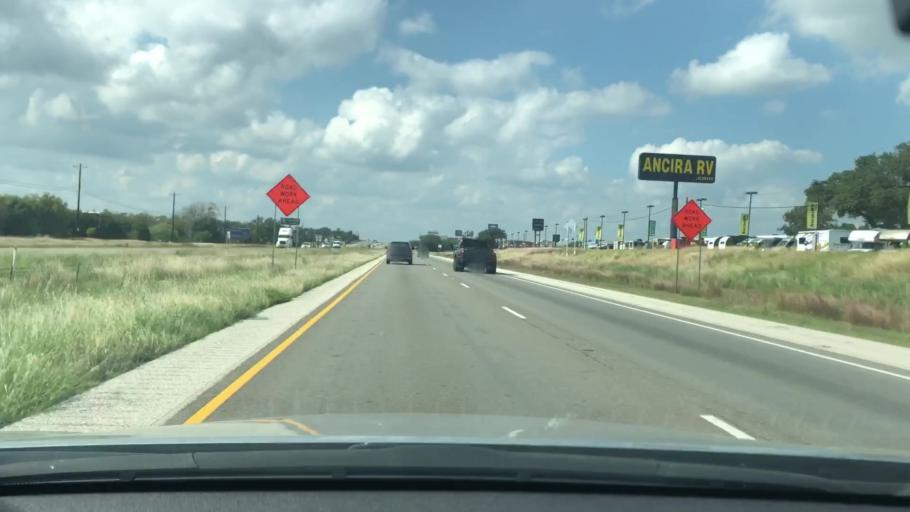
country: US
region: Texas
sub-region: Bexar County
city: Scenic Oaks
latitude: 29.7442
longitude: -98.6933
